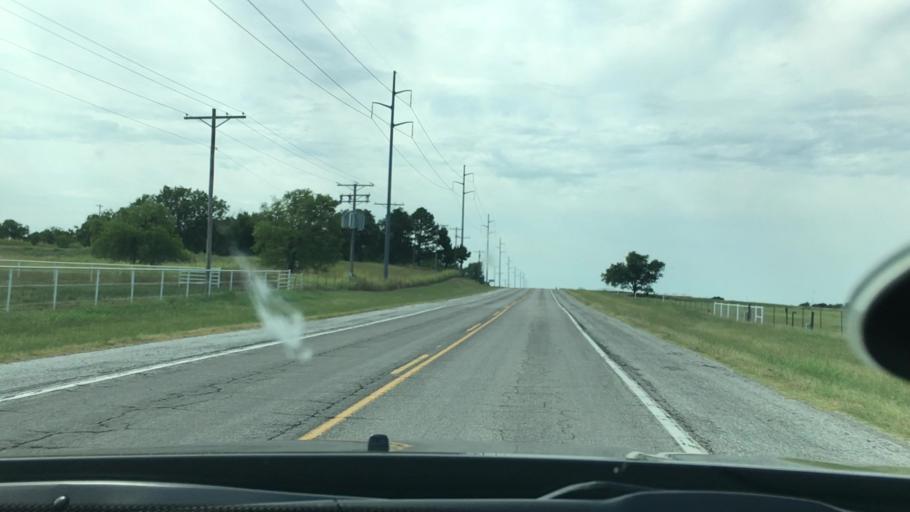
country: US
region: Oklahoma
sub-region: Carter County
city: Ardmore
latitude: 34.3279
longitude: -97.1430
